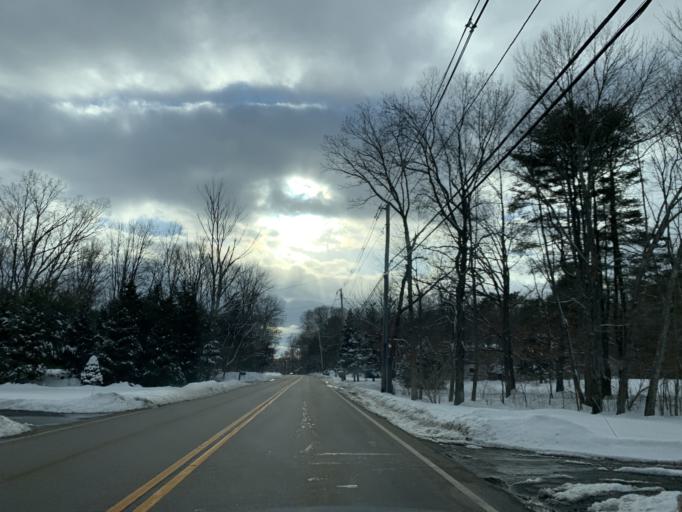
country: US
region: Massachusetts
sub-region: Norfolk County
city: Bellingham
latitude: 42.0415
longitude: -71.4480
